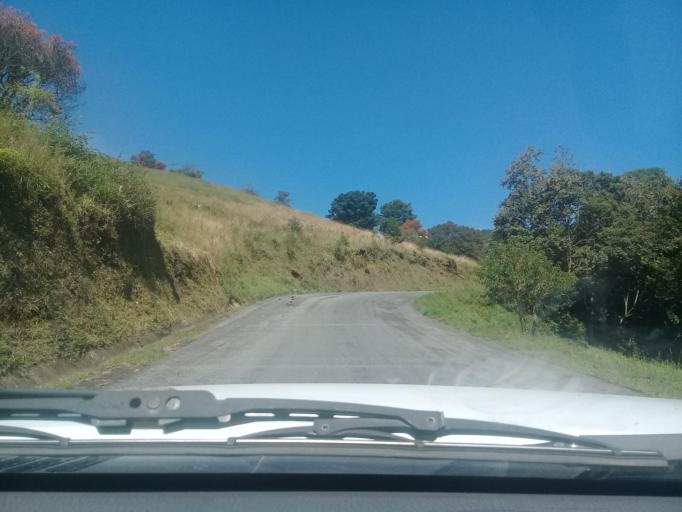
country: MX
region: Veracruz
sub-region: Tlalnelhuayocan
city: Otilpan
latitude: 19.5667
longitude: -96.9849
